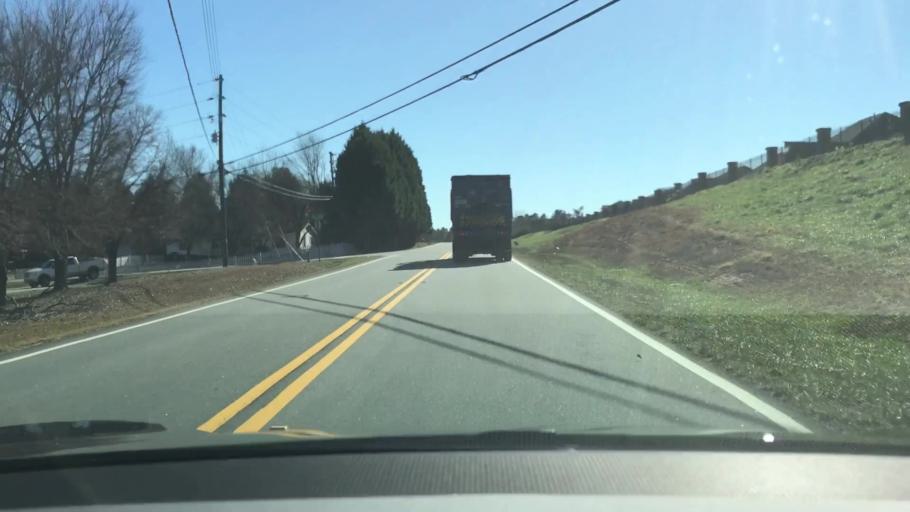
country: US
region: Georgia
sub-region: Barrow County
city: Auburn
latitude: 33.9276
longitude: -83.8282
